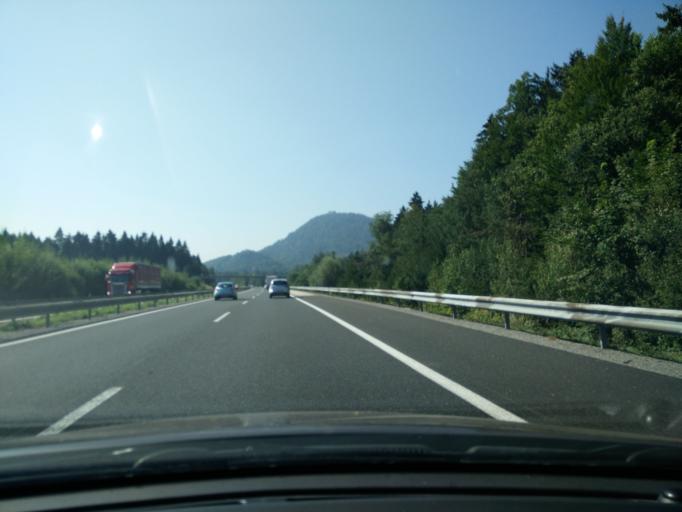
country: SI
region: Vodice
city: Vodice
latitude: 46.1518
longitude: 14.4780
